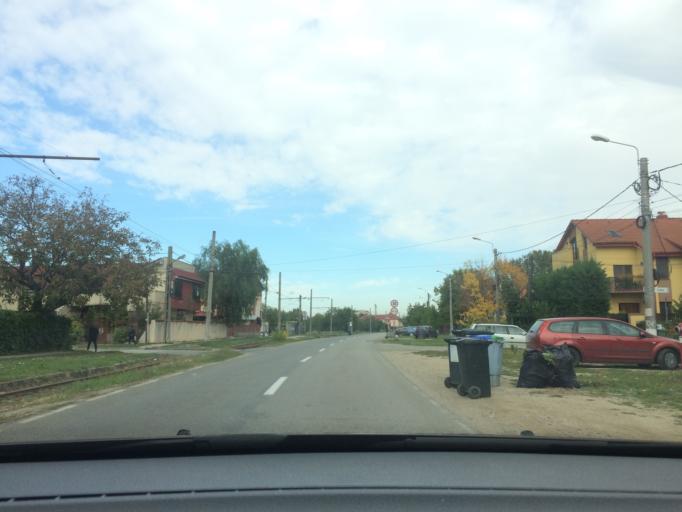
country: RO
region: Timis
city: Timisoara
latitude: 45.7551
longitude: 21.1916
